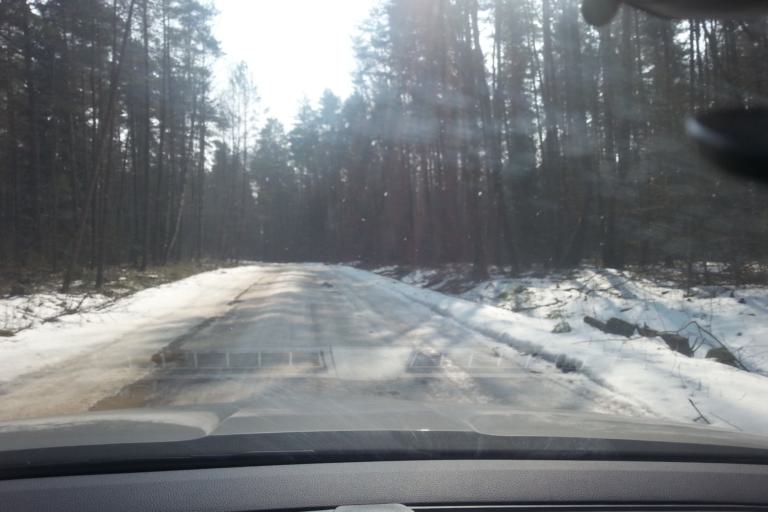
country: LT
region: Vilnius County
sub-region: Trakai
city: Rudiskes
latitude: 54.5104
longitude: 24.9342
